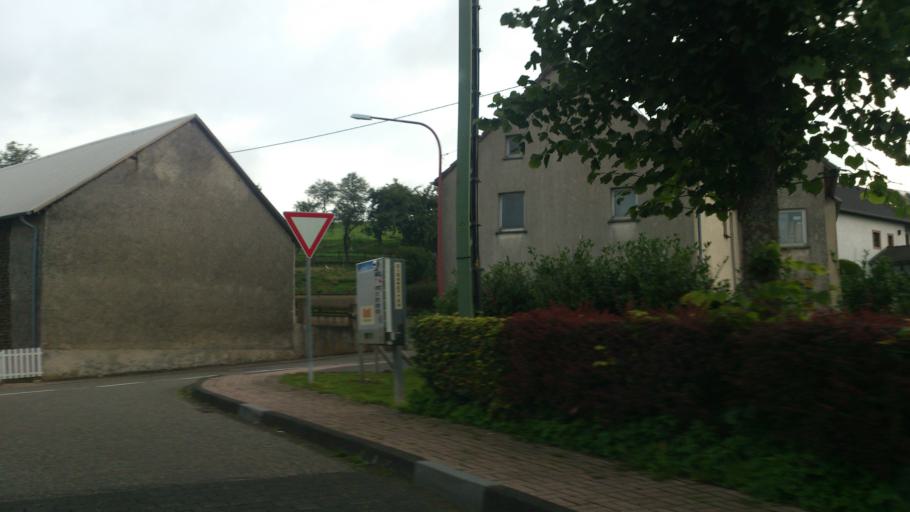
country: DE
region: Rheinland-Pfalz
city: Dreis-Bruck
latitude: 50.2752
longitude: 6.8099
